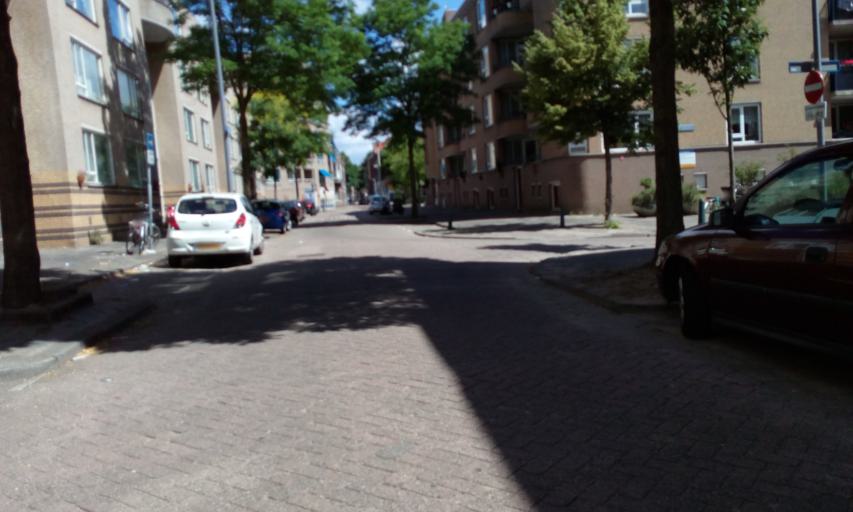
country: NL
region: South Holland
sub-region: Gemeente Rotterdam
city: Rotterdam
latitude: 51.9366
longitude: 4.4826
